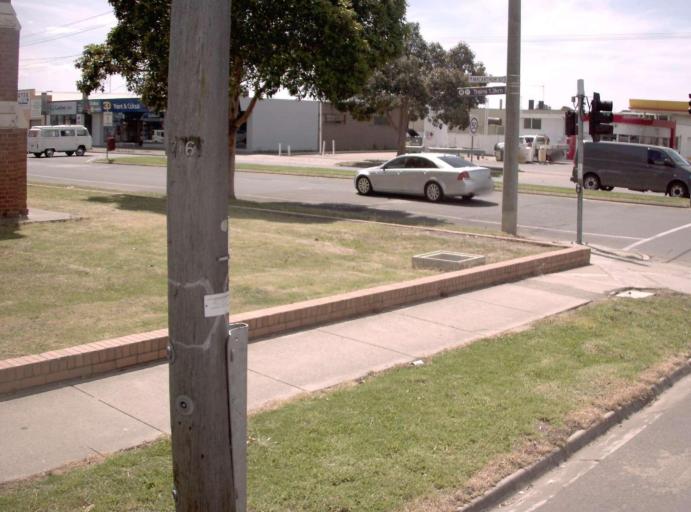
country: AU
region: Victoria
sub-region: Wellington
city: Sale
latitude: -38.1054
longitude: 147.0680
